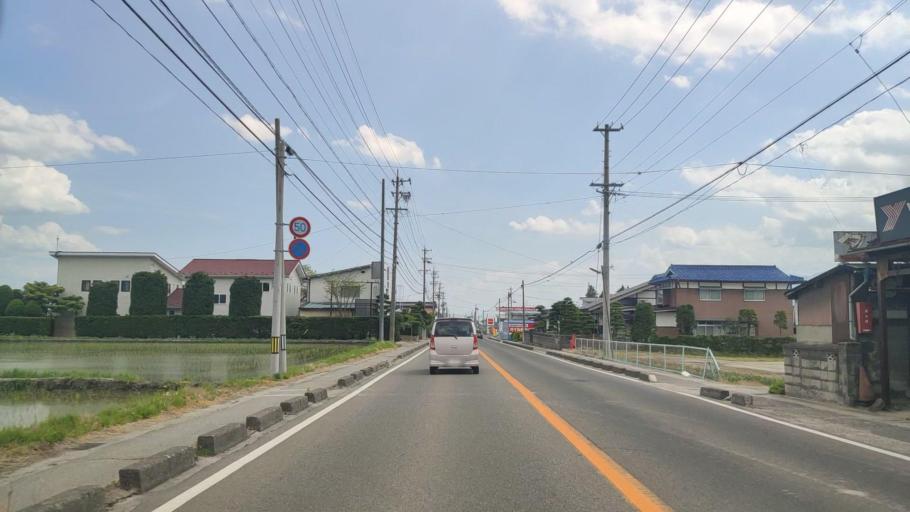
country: JP
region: Nagano
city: Omachi
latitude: 36.4706
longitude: 137.8486
